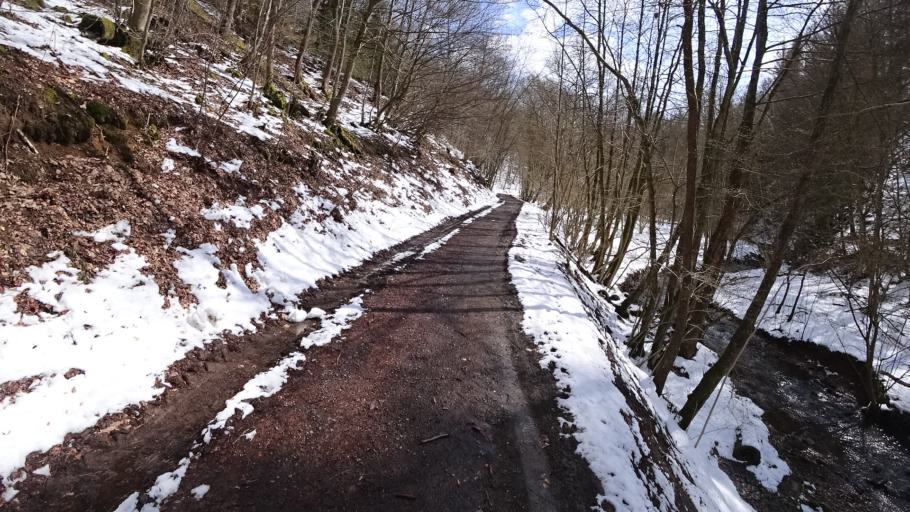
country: DE
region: Rheinland-Pfalz
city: Kausen
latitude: 50.7368
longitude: 7.8643
